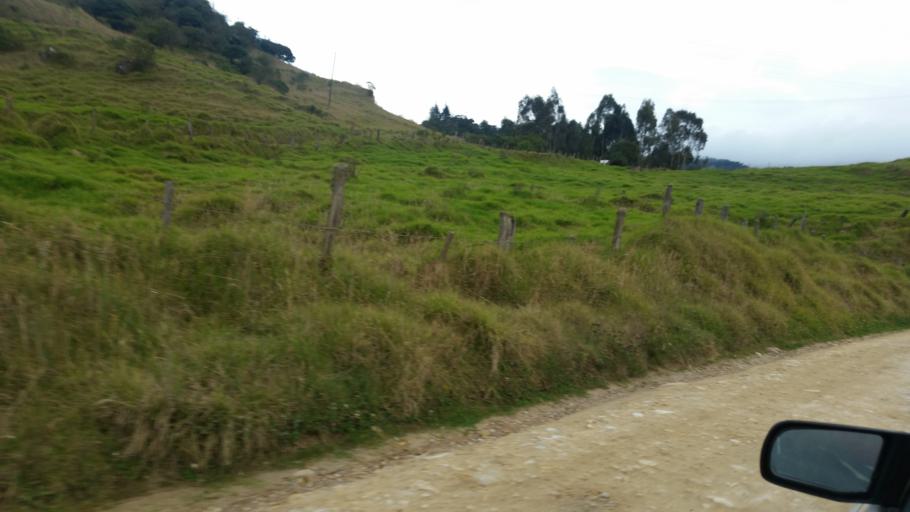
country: CO
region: Cundinamarca
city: La Calera
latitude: 4.7141
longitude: -73.9453
